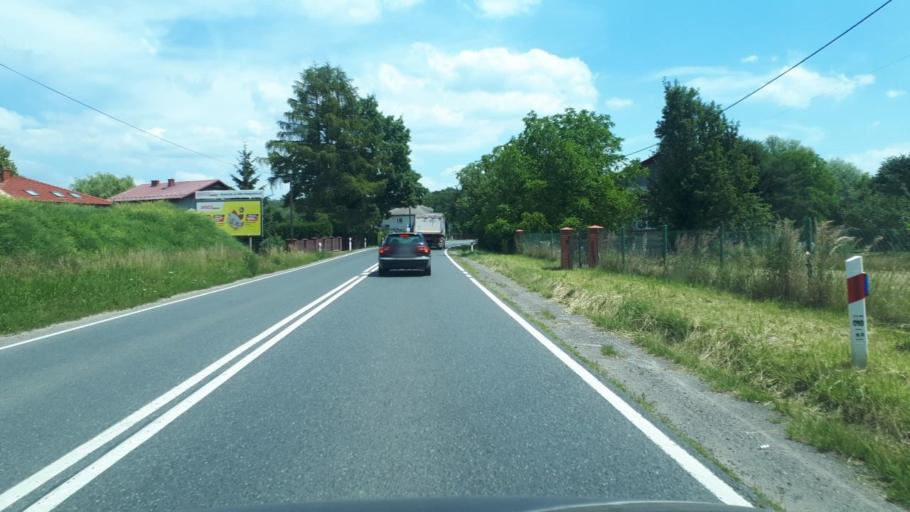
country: PL
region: Silesian Voivodeship
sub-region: Powiat pszczynski
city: Gora
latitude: 49.9749
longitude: 19.1208
